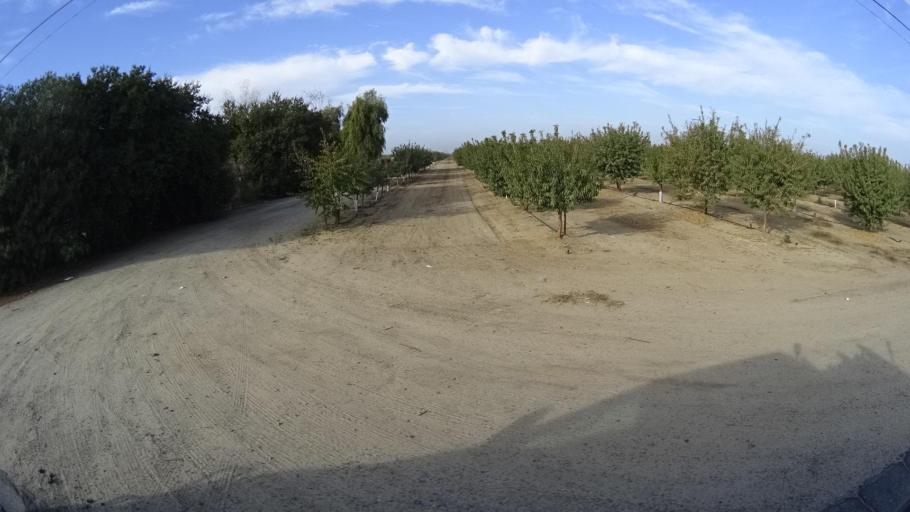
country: US
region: California
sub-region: Kern County
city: Delano
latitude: 35.7580
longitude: -119.2053
